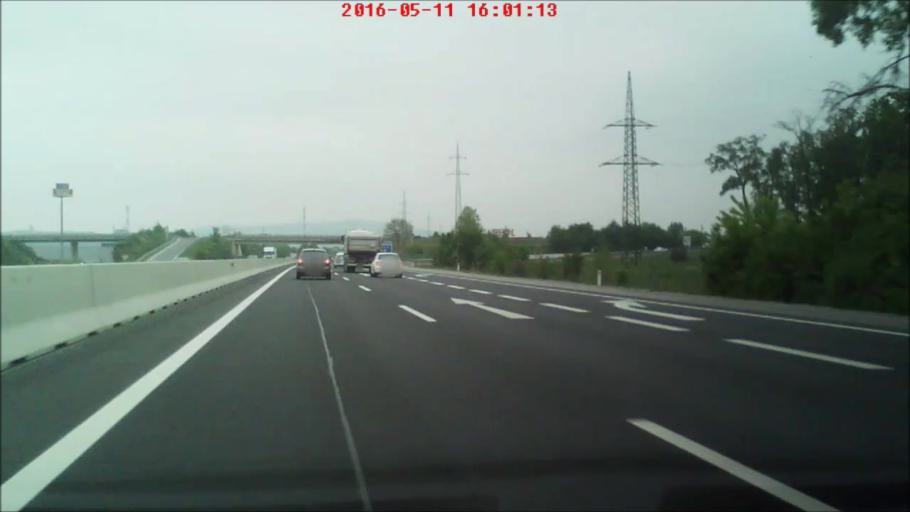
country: AT
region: Styria
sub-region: Politischer Bezirk Graz-Umgebung
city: Wundschuh
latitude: 46.9363
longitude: 15.4607
